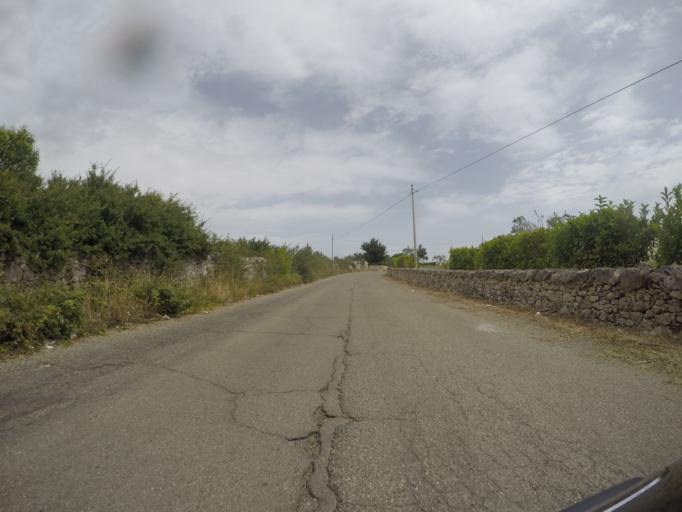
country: IT
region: Apulia
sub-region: Provincia di Taranto
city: Martina Franca
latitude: 40.6855
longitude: 17.3429
